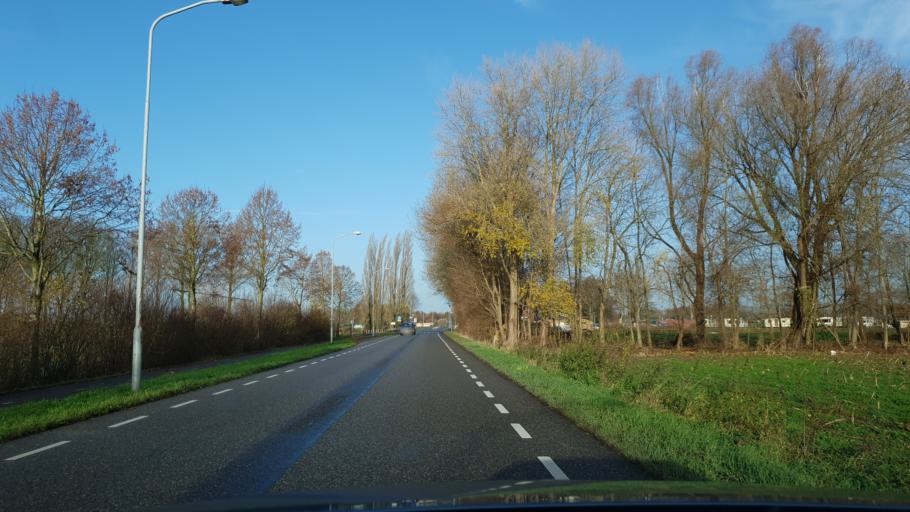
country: NL
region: Gelderland
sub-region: Gemeente Wijchen
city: Bergharen
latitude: 51.8422
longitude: 5.6730
